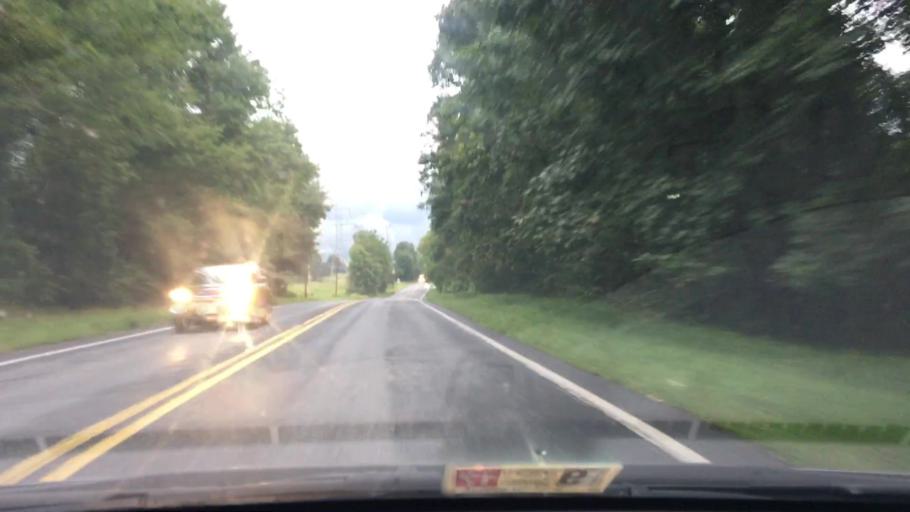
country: US
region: Maryland
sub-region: Montgomery County
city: Redland
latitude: 39.1852
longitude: -77.1372
